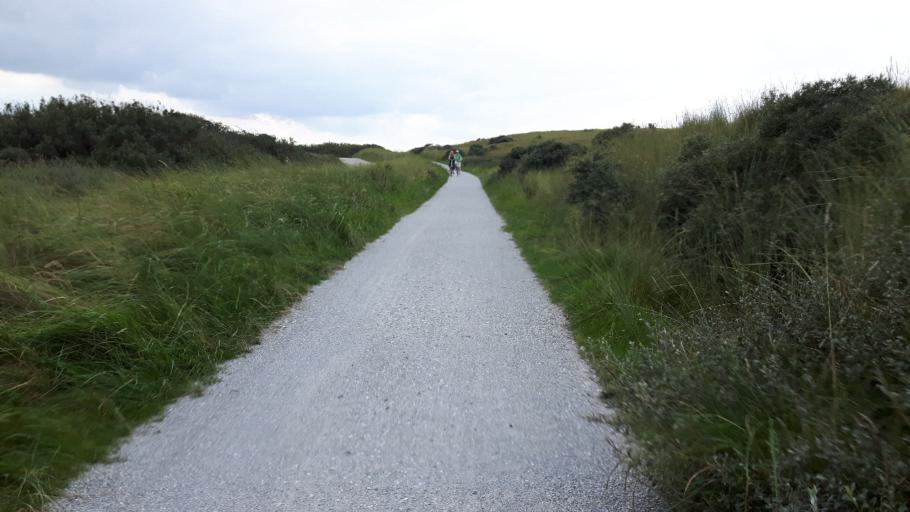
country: NL
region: Friesland
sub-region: Gemeente Ameland
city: Nes
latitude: 53.4600
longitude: 5.8332
